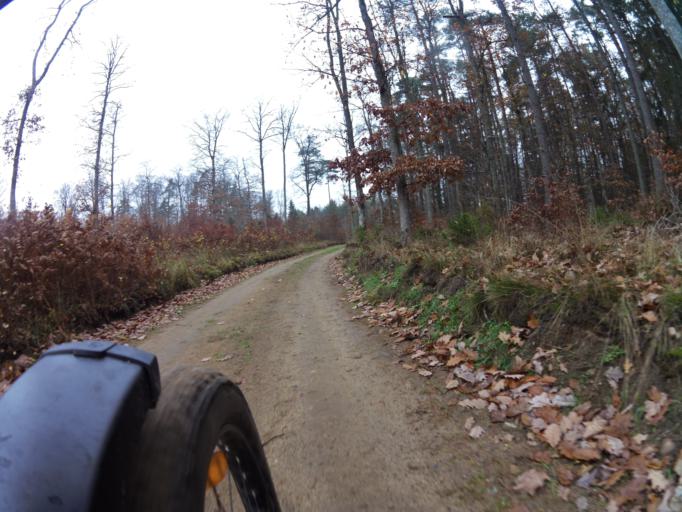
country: PL
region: Pomeranian Voivodeship
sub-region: Powiat wejherowski
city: Orle
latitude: 54.6969
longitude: 18.1566
